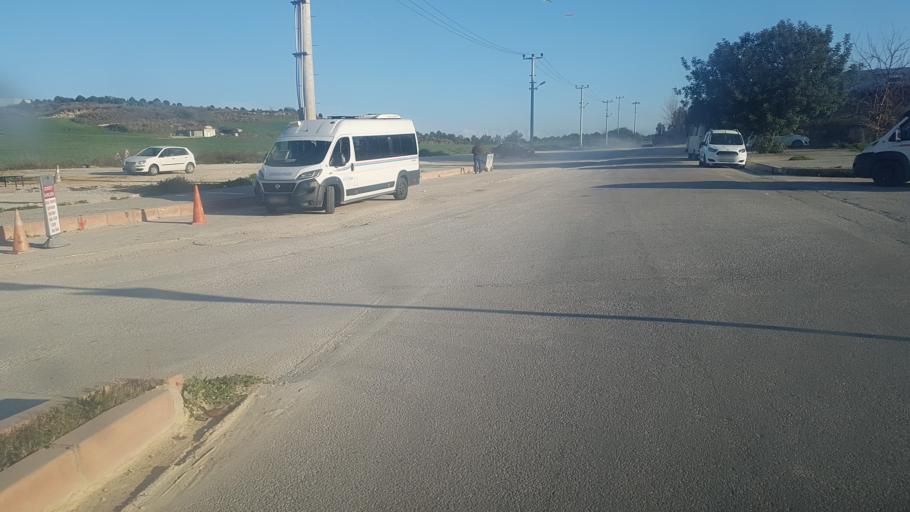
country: TR
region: Adana
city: Seyhan
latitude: 37.0529
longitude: 35.2532
